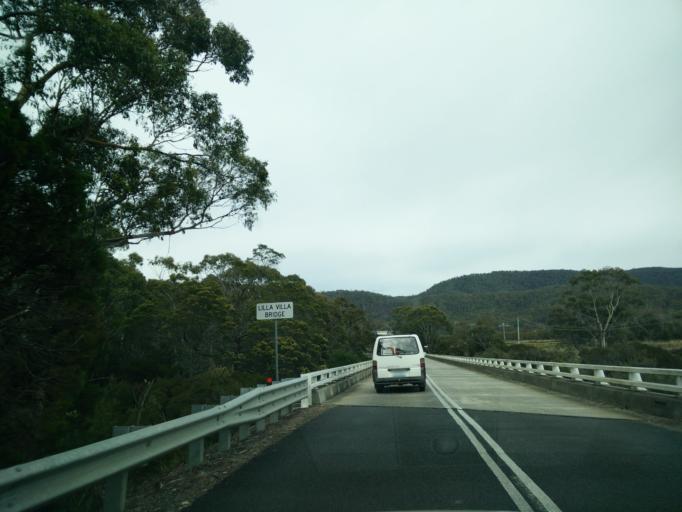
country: AU
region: Tasmania
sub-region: Break O'Day
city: St Helens
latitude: -41.8952
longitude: 148.2589
